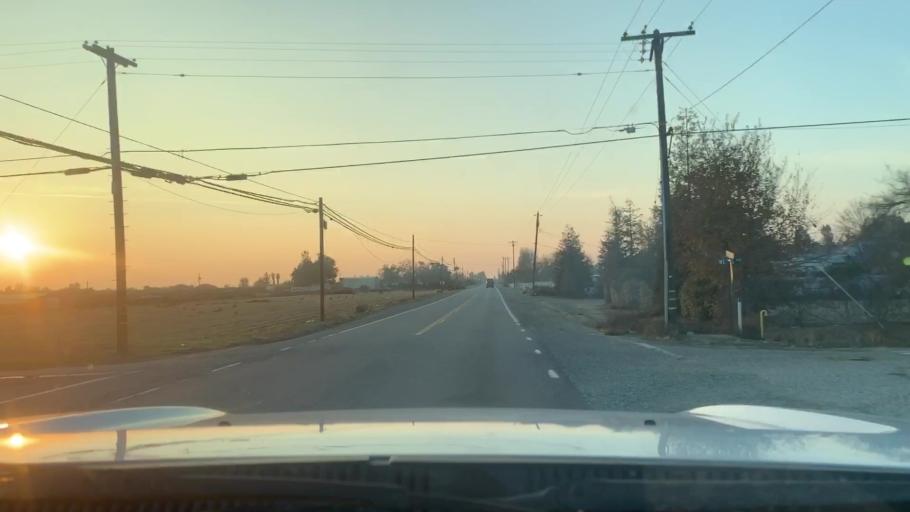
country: US
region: California
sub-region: Kern County
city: Rosedale
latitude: 35.3835
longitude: -119.1899
